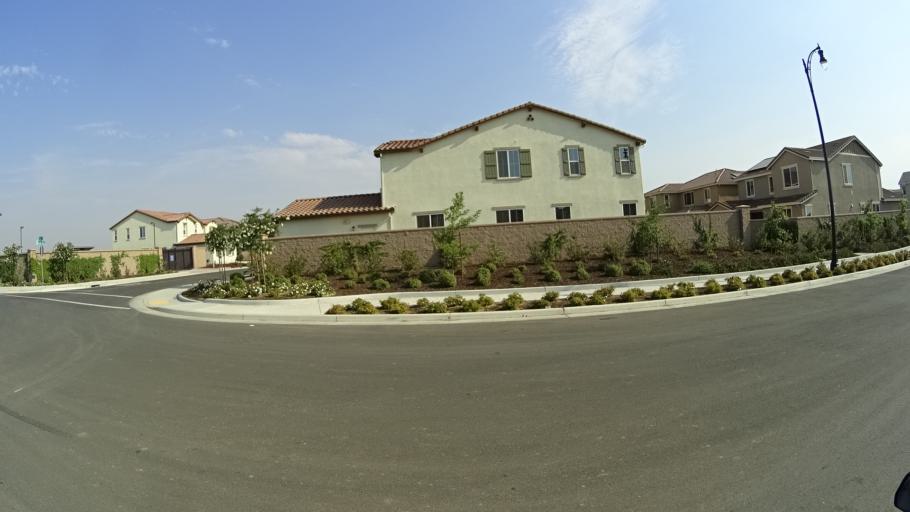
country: US
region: California
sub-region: Sacramento County
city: Elk Grove
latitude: 38.3837
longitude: -121.3798
